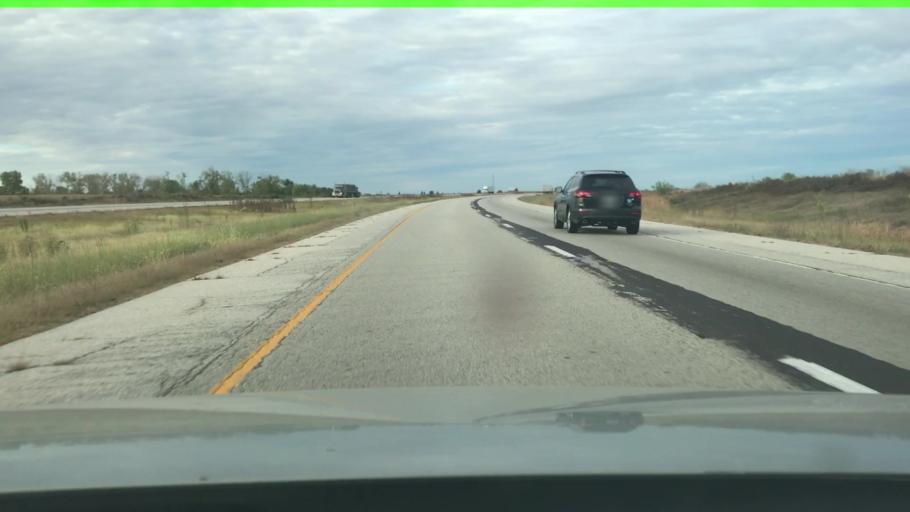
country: US
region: Illinois
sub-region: Livingston County
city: Odell
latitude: 41.0269
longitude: -88.5050
